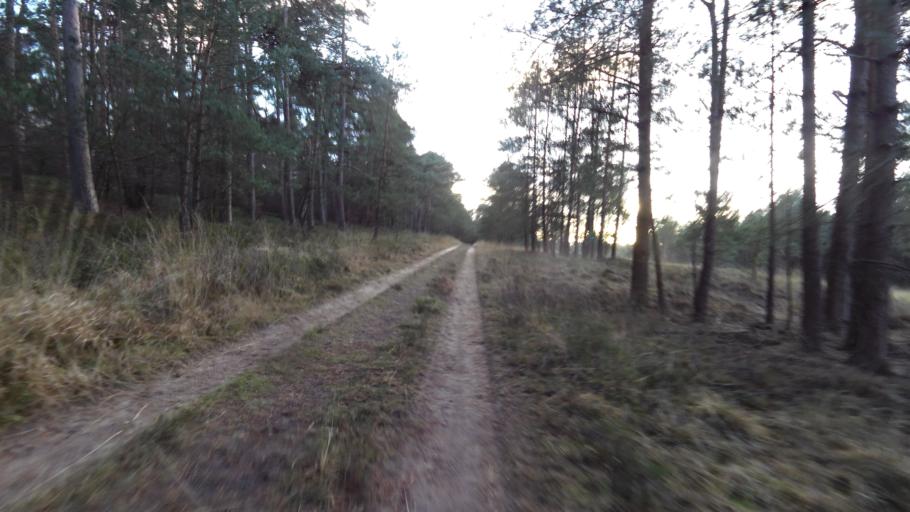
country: NL
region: Gelderland
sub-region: Gemeente Apeldoorn
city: Uddel
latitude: 52.3113
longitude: 5.8580
